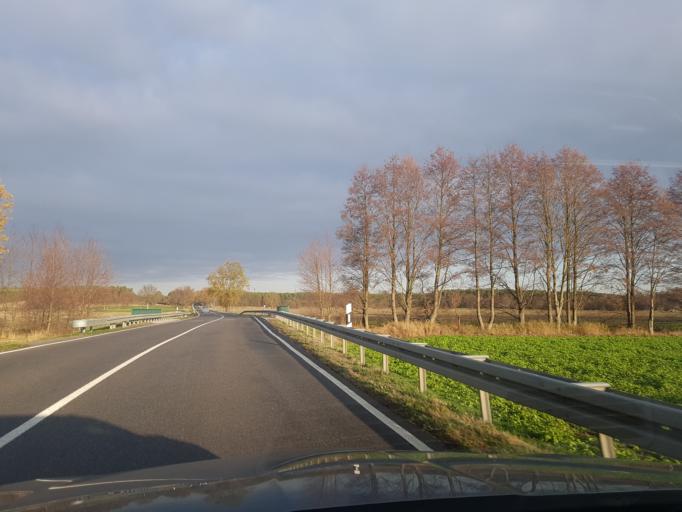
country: DE
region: Brandenburg
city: Kasel-Golzig
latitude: 51.9037
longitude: 13.6745
